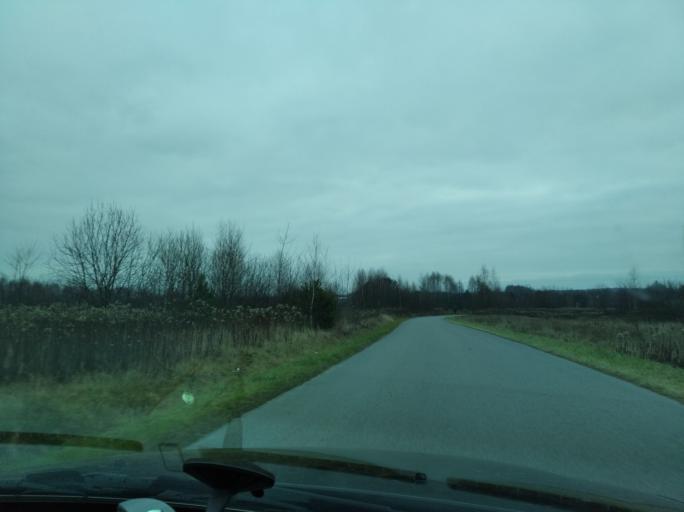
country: PL
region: Subcarpathian Voivodeship
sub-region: Powiat lancucki
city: Brzoza Stadnicka
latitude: 50.2019
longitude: 22.2790
